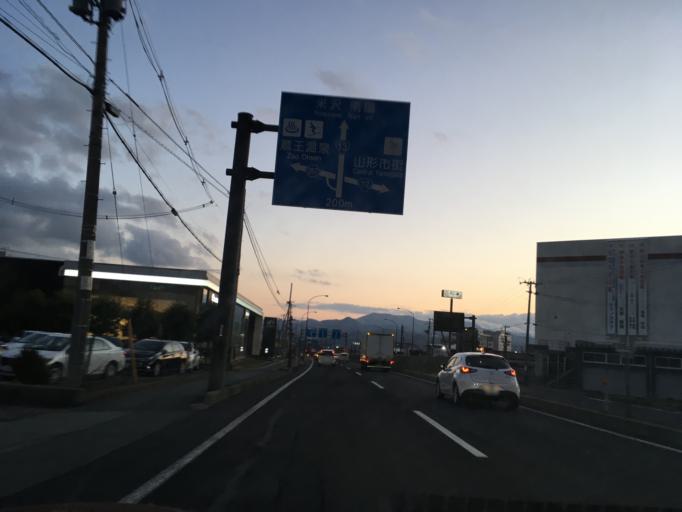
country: JP
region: Yamagata
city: Yamagata-shi
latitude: 38.2176
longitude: 140.3273
